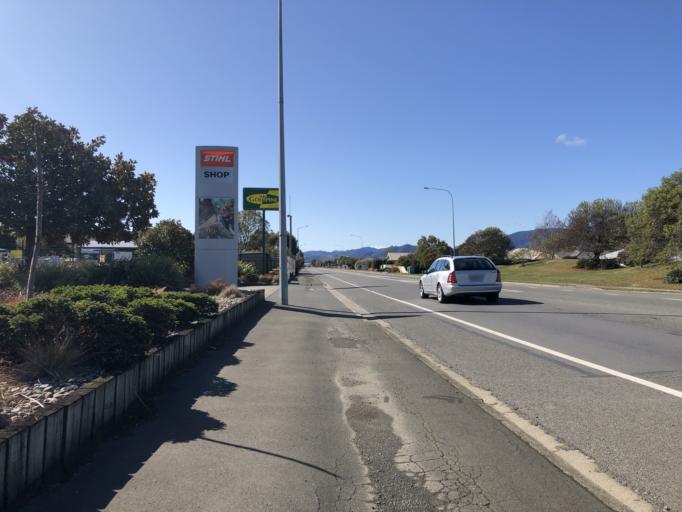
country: NZ
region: Tasman
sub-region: Tasman District
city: Richmond
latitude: -41.3439
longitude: 173.1699
